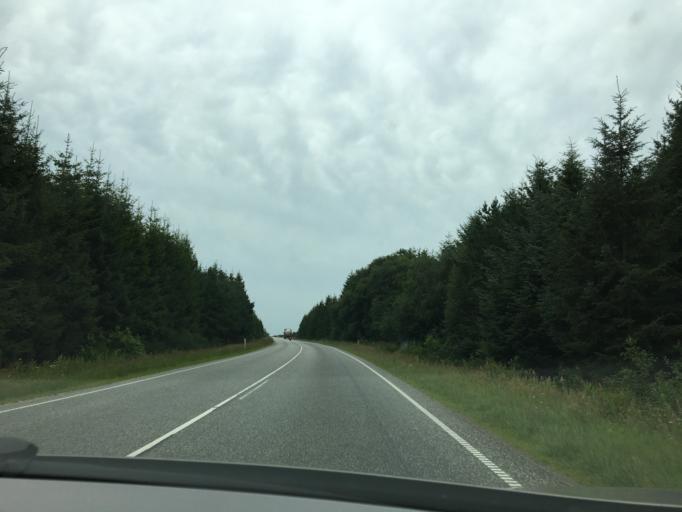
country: DK
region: Central Jutland
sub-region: Herning Kommune
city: Sunds
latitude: 56.3531
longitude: 8.9727
